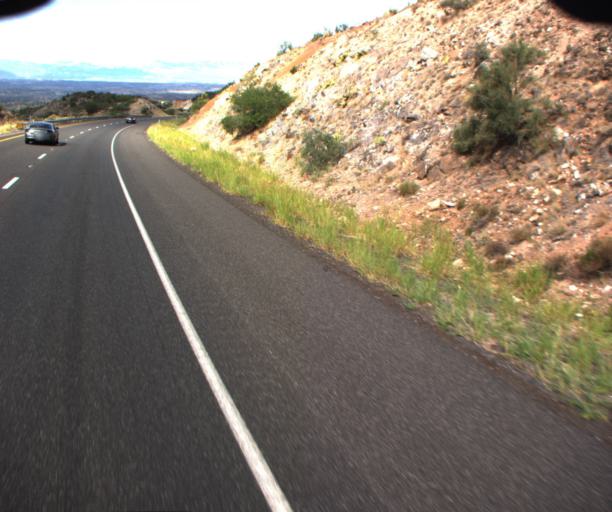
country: US
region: Arizona
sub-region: Yavapai County
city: Big Park
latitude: 34.7110
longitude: -111.7323
